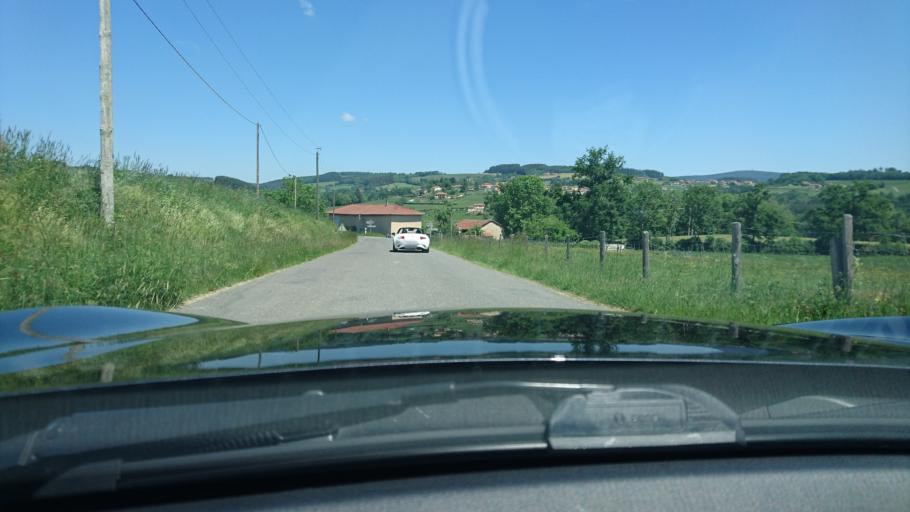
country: FR
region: Rhone-Alpes
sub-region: Departement de la Loire
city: Rozier-en-Donzy
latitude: 45.8181
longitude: 4.3065
